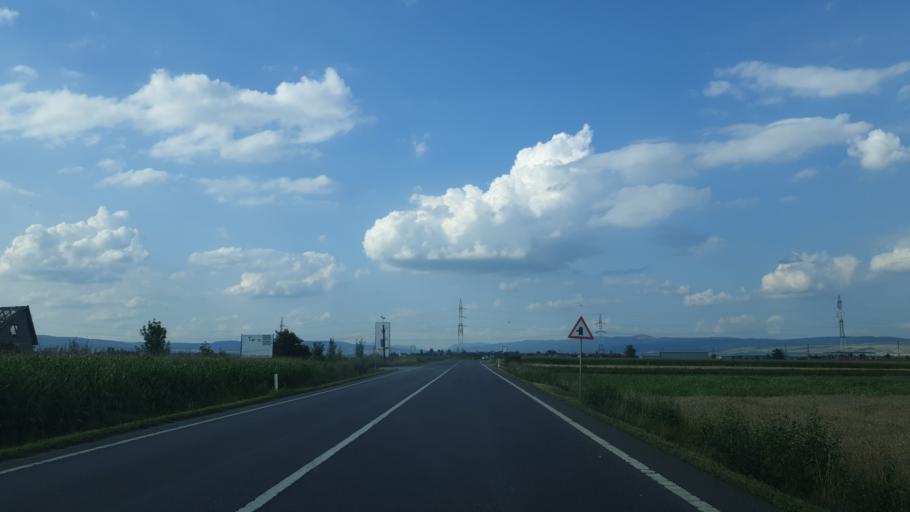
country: RO
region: Covasna
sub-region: Comuna Chichis
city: Chichis
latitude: 45.8229
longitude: 25.7999
